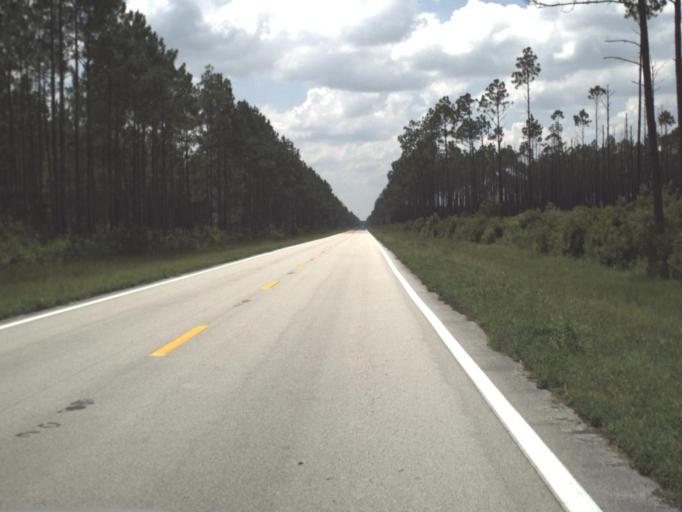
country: US
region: Florida
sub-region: Baker County
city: Macclenny
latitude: 30.5513
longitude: -82.3618
